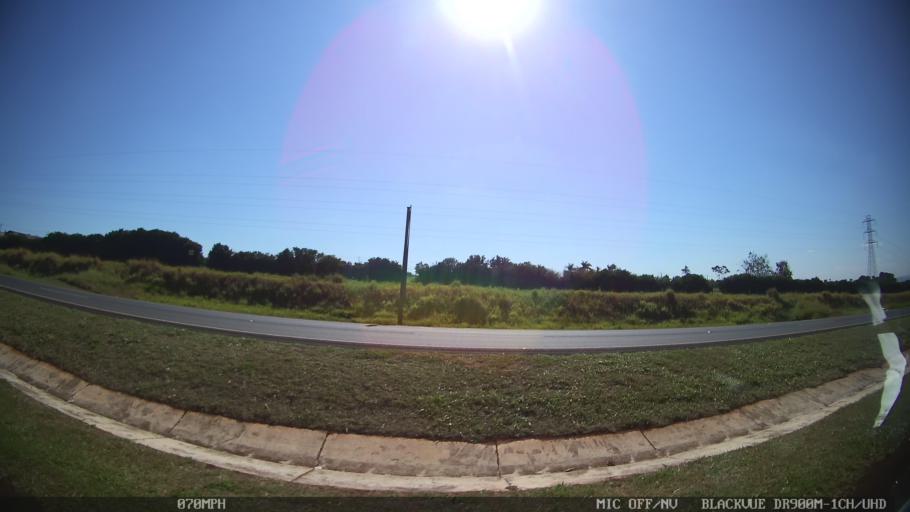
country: BR
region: Sao Paulo
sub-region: Ribeirao Preto
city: Ribeirao Preto
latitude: -21.1224
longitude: -47.8367
